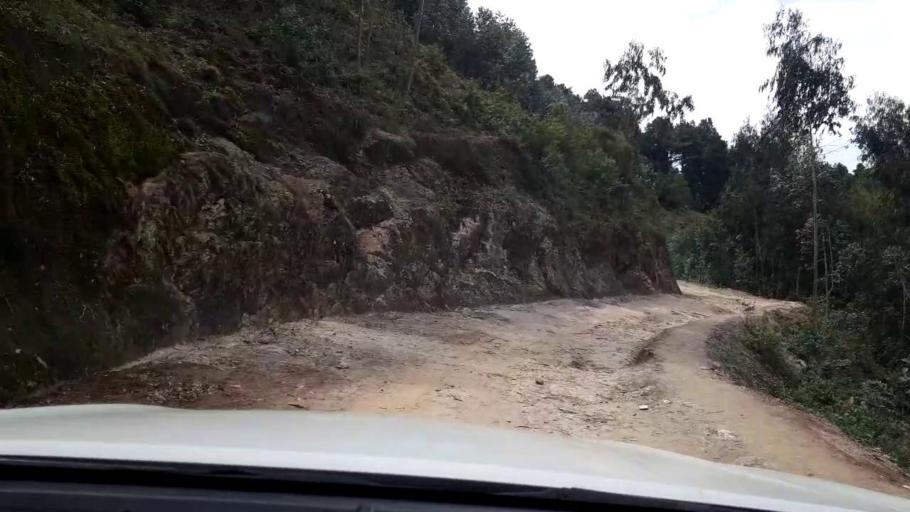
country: RW
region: Western Province
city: Kibuye
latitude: -1.8757
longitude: 29.4535
